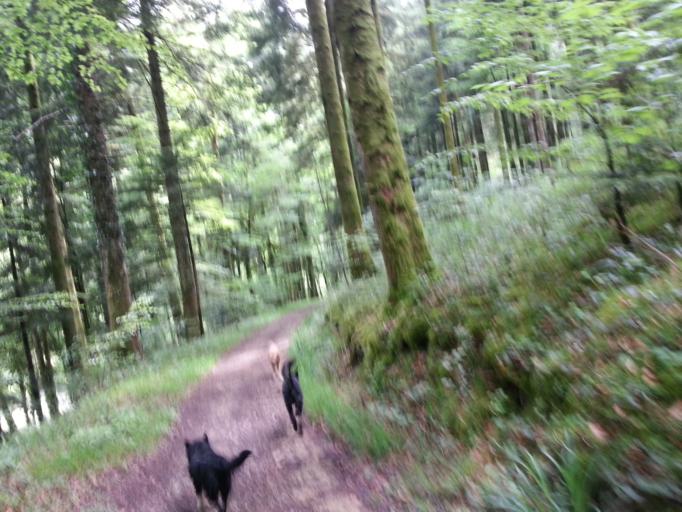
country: FR
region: Franche-Comte
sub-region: Departement du Jura
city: Salins-les-Bains
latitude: 46.9997
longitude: 5.9975
